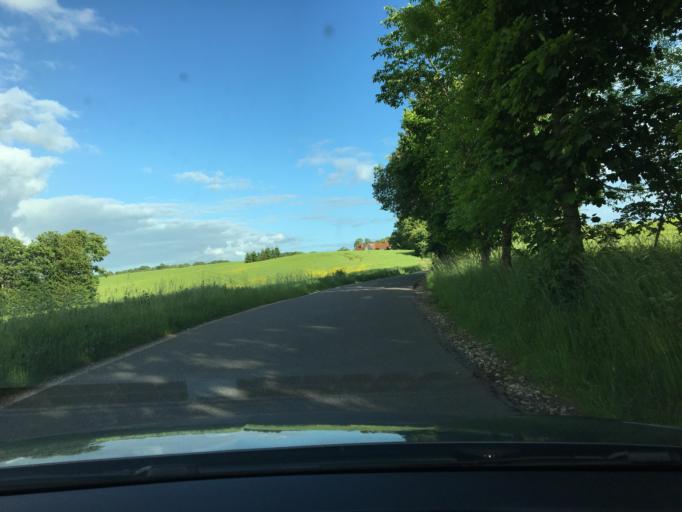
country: DK
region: Central Jutland
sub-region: Favrskov Kommune
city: Hinnerup
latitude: 56.3030
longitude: 10.1029
